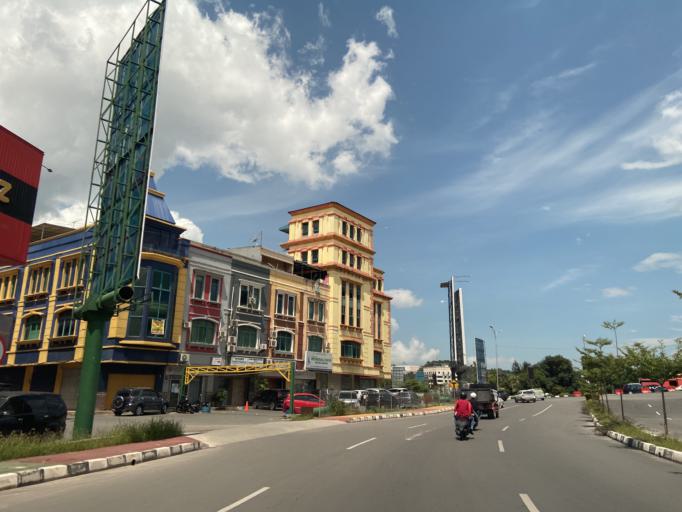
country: SG
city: Singapore
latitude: 1.1328
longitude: 104.0176
